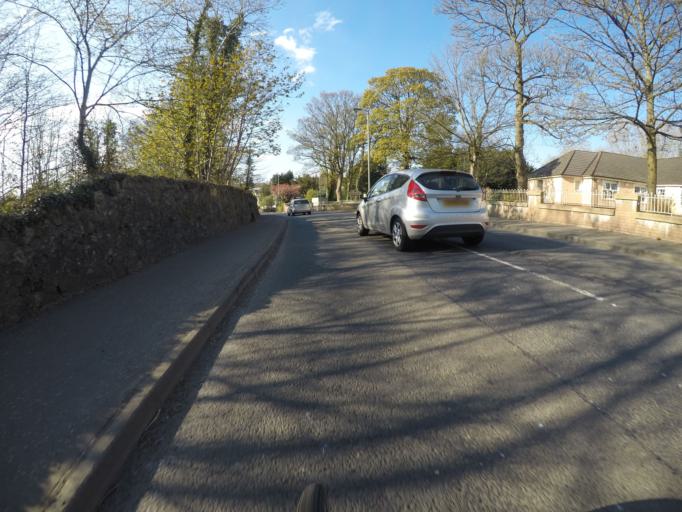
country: GB
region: Scotland
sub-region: North Ayrshire
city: Kilwinning
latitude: 55.6511
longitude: -4.6895
